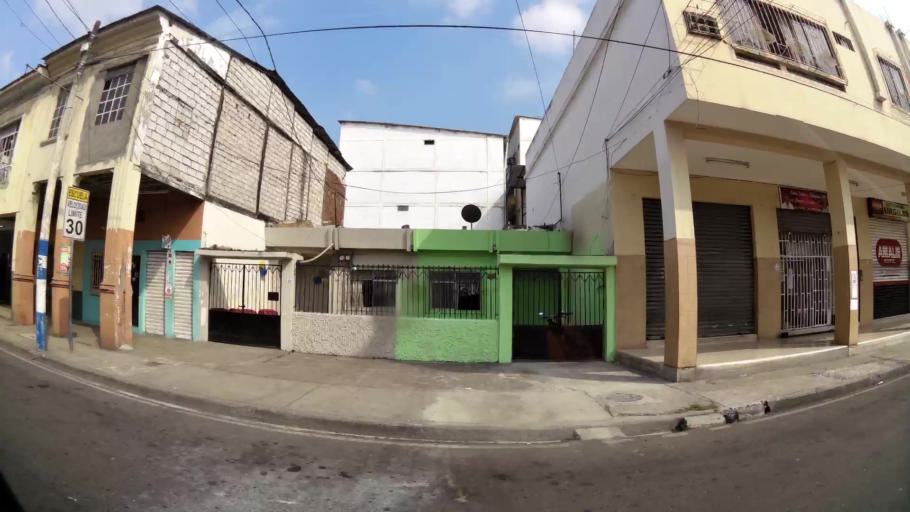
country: EC
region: Guayas
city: Guayaquil
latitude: -2.2035
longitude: -79.9014
